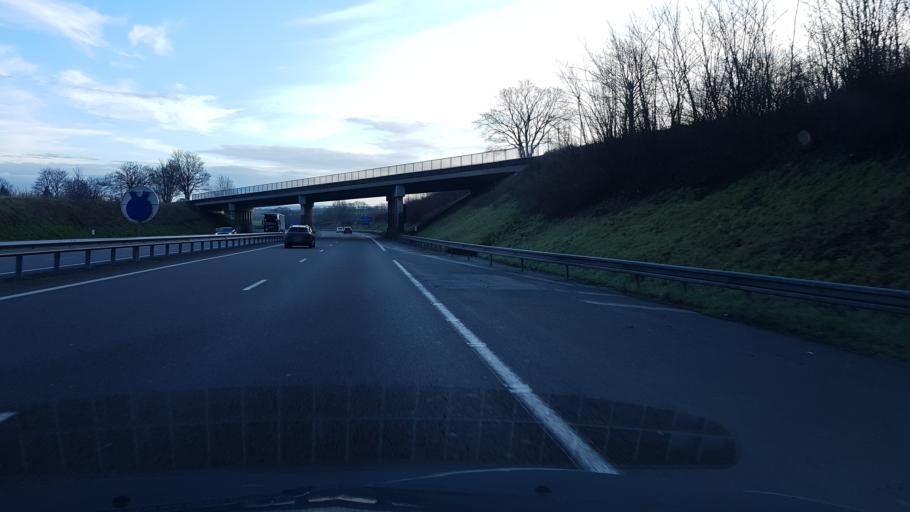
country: FR
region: Lorraine
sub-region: Departement de Meurthe-et-Moselle
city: Valleroy
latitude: 49.1994
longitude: 5.9330
